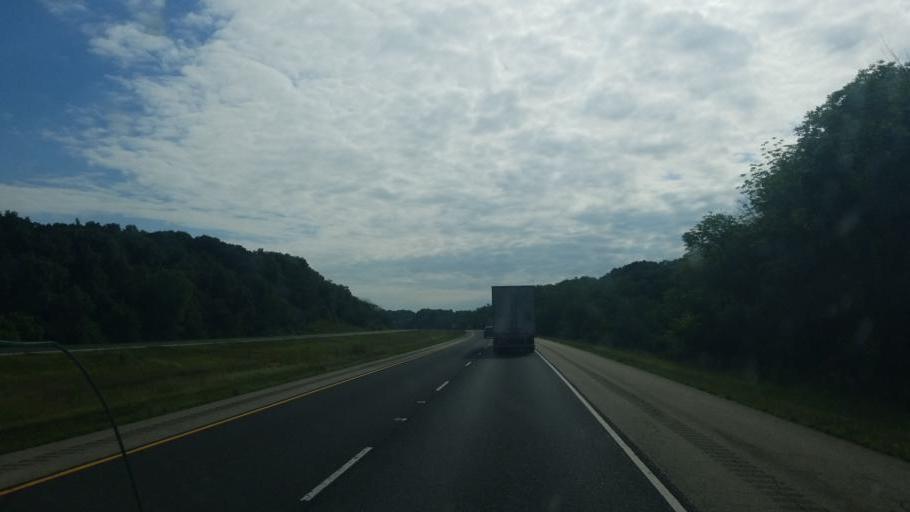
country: US
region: Illinois
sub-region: Clark County
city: Marshall
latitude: 39.4028
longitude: -87.7427
